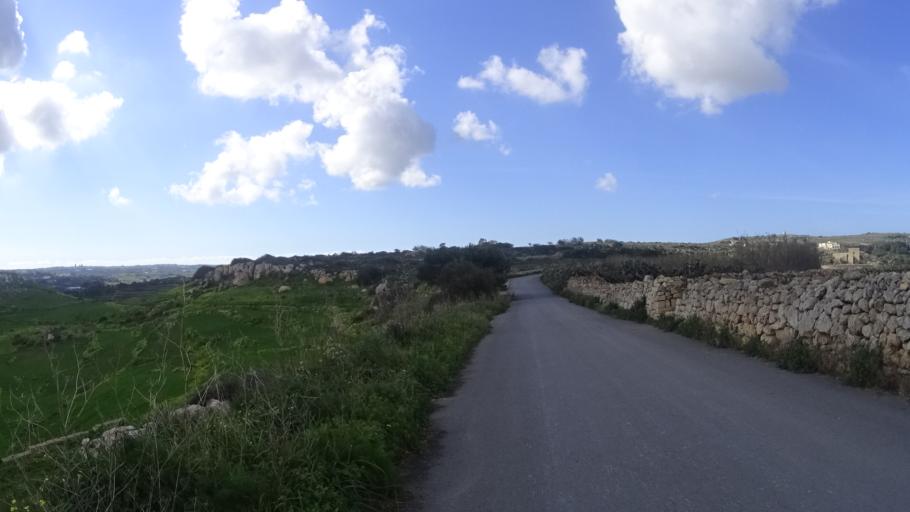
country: MT
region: L-Imtarfa
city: Imtarfa
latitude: 35.9029
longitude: 14.3847
